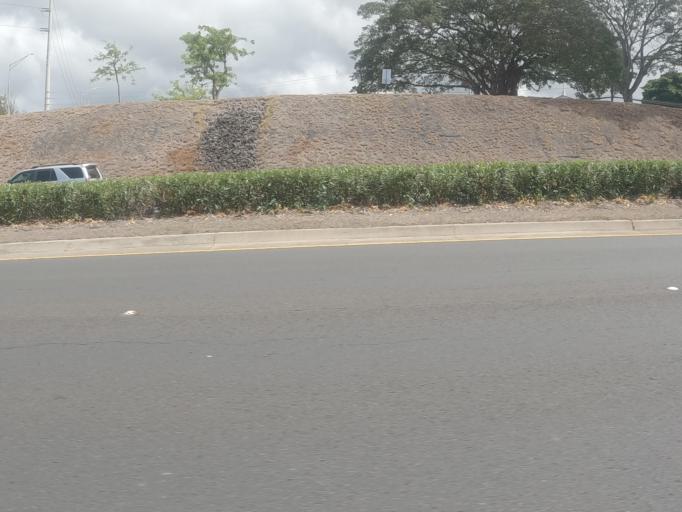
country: US
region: Hawaii
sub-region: Honolulu County
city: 'Aiea
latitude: 21.3756
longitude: -157.9303
